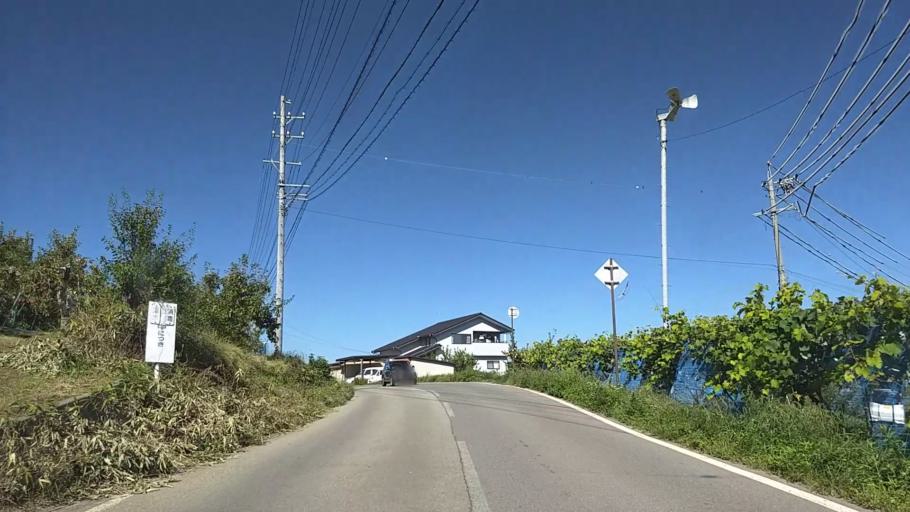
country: JP
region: Nagano
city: Nagano-shi
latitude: 36.5789
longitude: 138.1256
